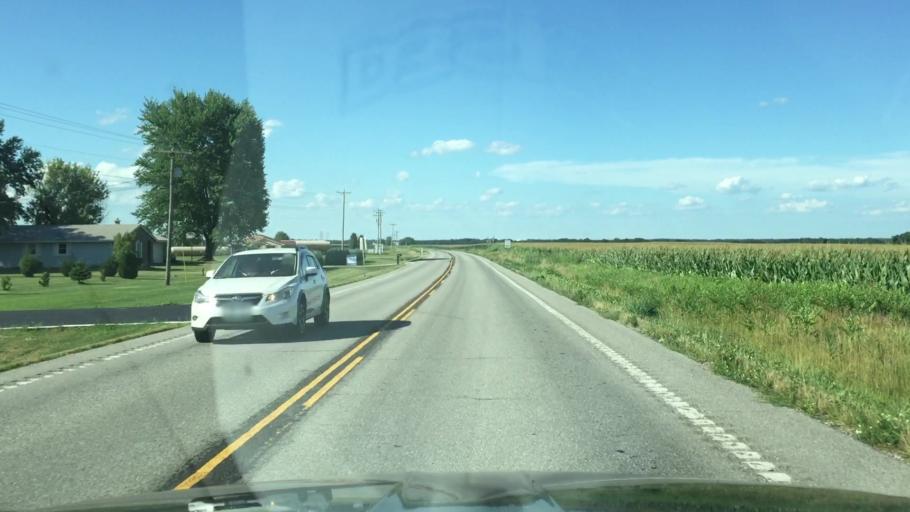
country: US
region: Missouri
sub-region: Moniteau County
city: Tipton
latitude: 38.5756
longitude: -92.7931
